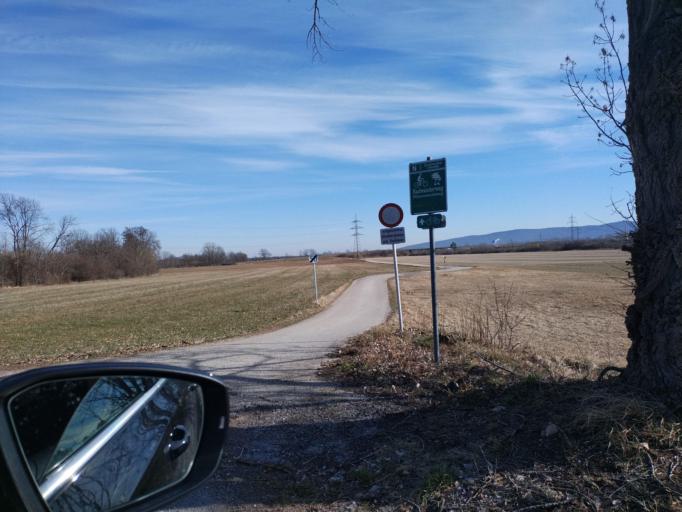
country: AT
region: Lower Austria
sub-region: Politischer Bezirk Neunkirchen
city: Breitenau
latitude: 47.7393
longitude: 16.1682
